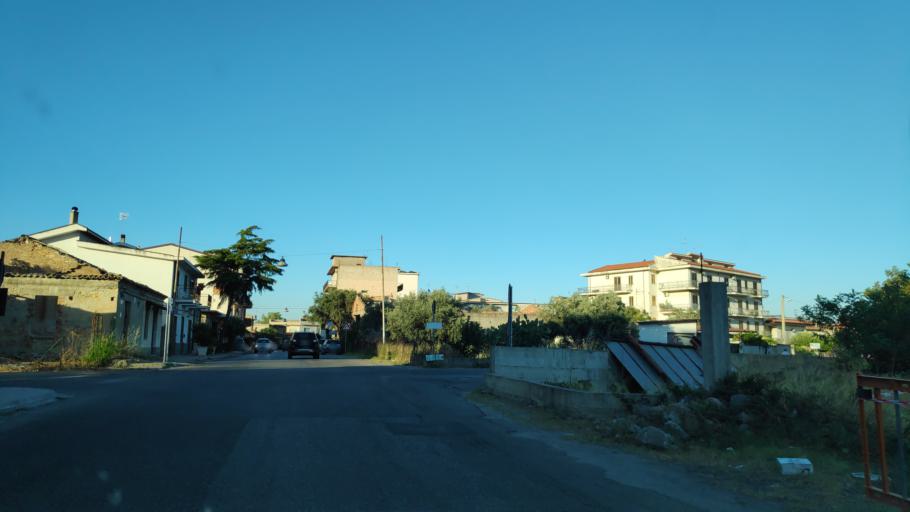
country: IT
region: Calabria
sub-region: Provincia di Reggio Calabria
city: Locri
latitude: 38.2385
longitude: 16.2519
